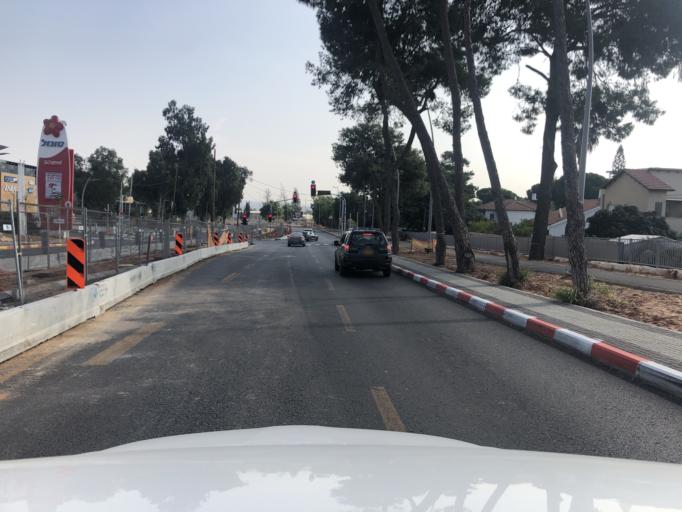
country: IL
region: Central District
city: Kfar Saba
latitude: 32.1706
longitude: 34.9256
